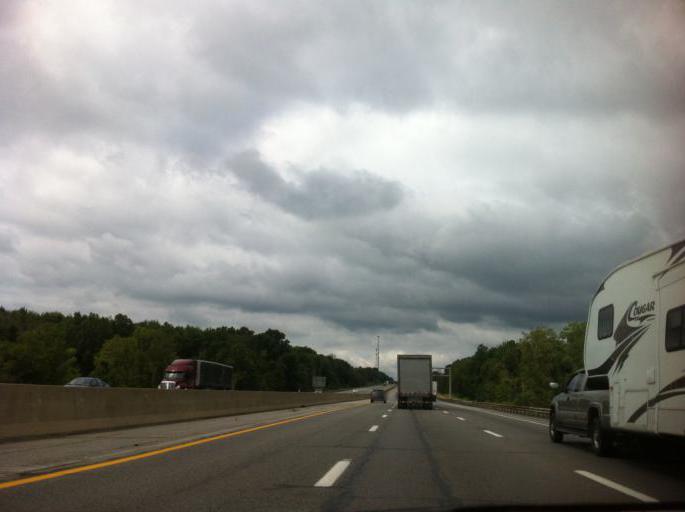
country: US
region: Ohio
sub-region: Portage County
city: Mantua
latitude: 41.2437
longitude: -81.1955
